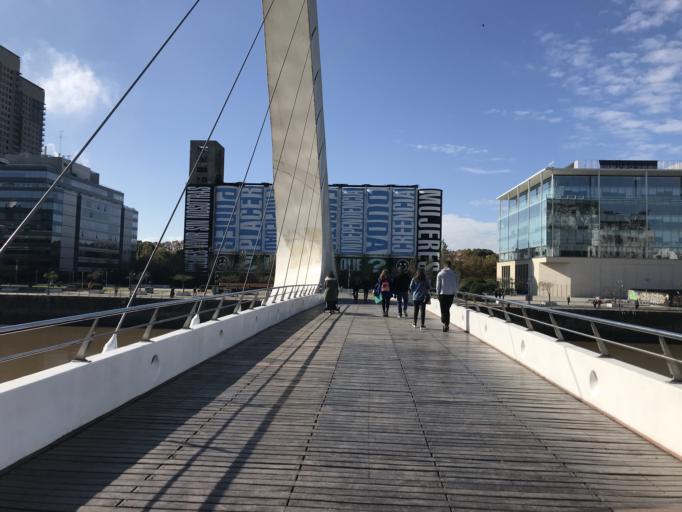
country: AR
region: Buenos Aires F.D.
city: Buenos Aires
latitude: -34.6080
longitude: -58.3652
